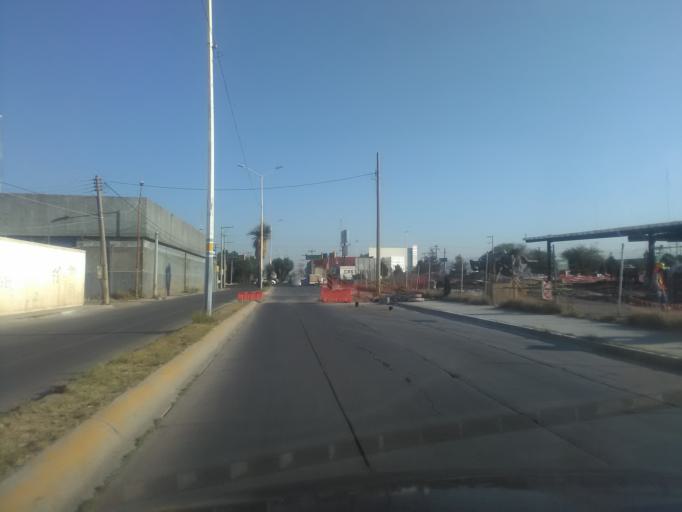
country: MX
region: Durango
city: Victoria de Durango
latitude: 24.0458
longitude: -104.6232
